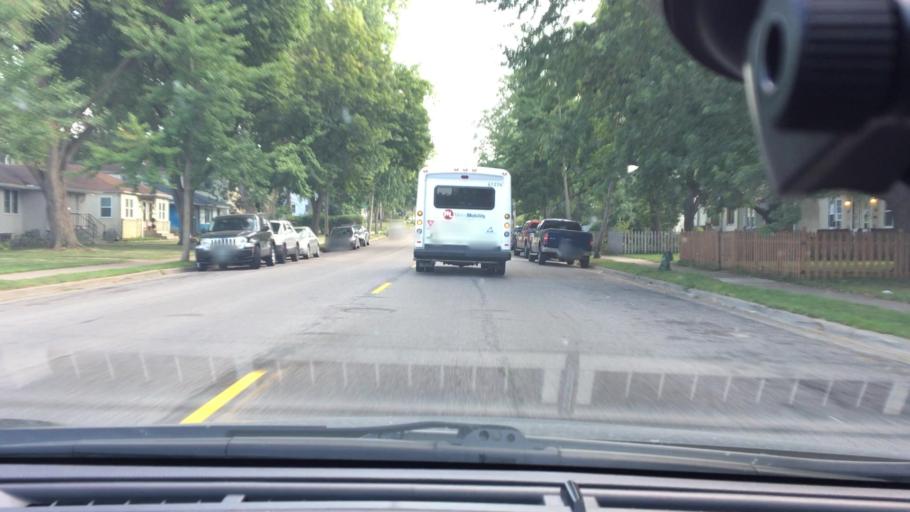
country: US
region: Minnesota
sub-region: Hennepin County
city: Richfield
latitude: 44.9262
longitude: -93.2524
